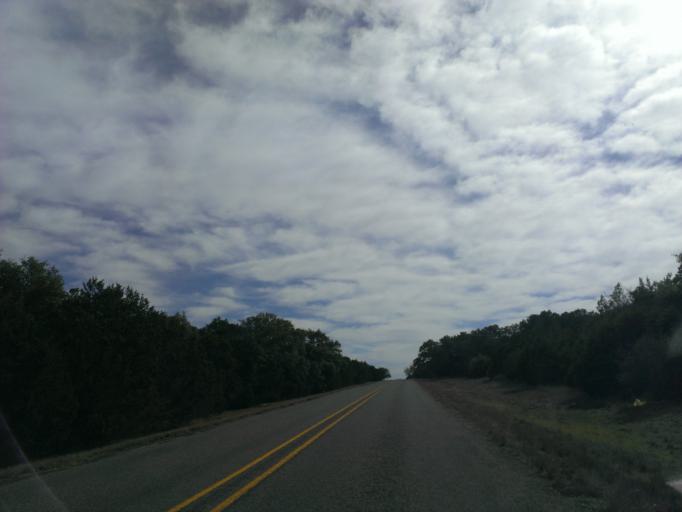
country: US
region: Texas
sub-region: Llano County
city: Buchanan Dam
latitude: 30.6929
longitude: -98.3552
